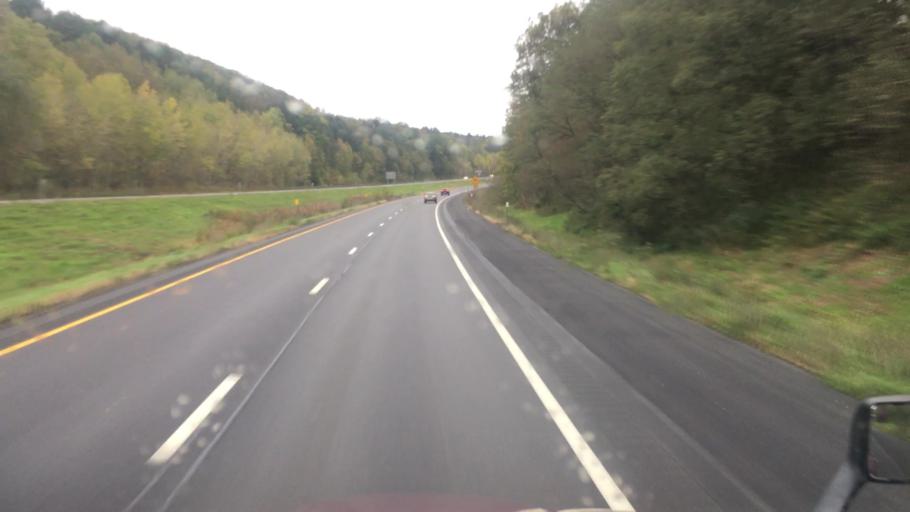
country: US
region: New York
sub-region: Otsego County
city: Unadilla
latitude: 42.3099
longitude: -75.3368
